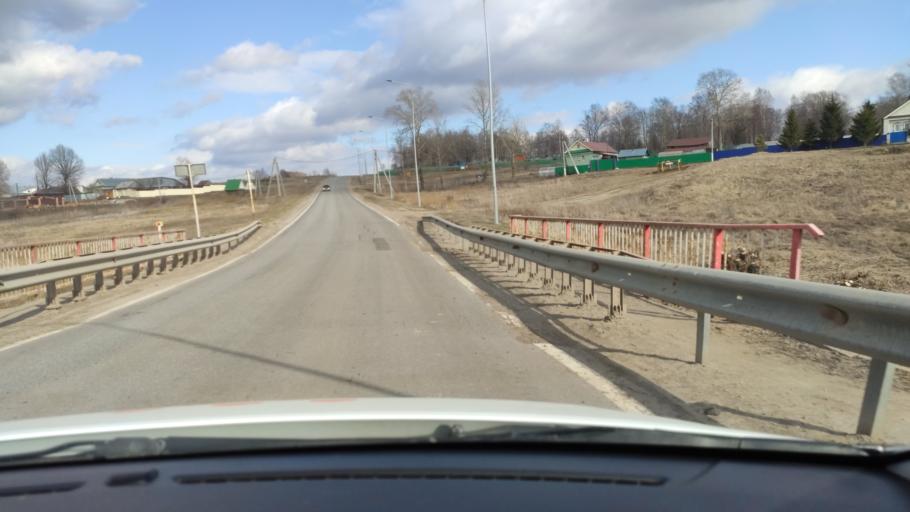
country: RU
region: Tatarstan
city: Vysokaya Gora
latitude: 56.2209
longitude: 49.2755
